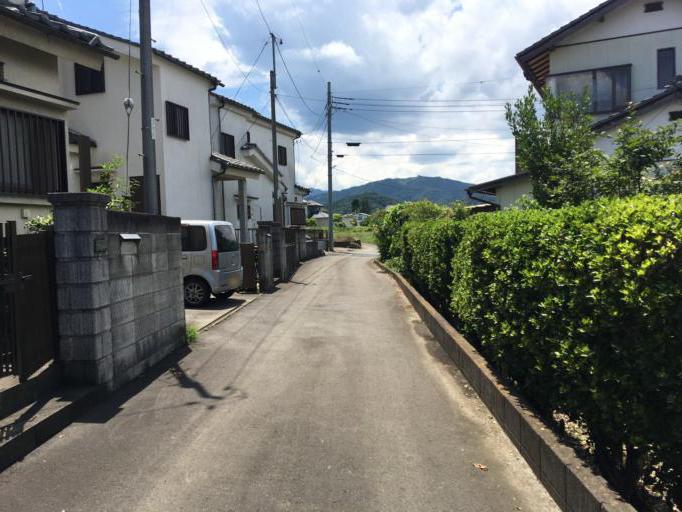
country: JP
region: Saitama
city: Ogawa
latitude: 36.0045
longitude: 139.2942
